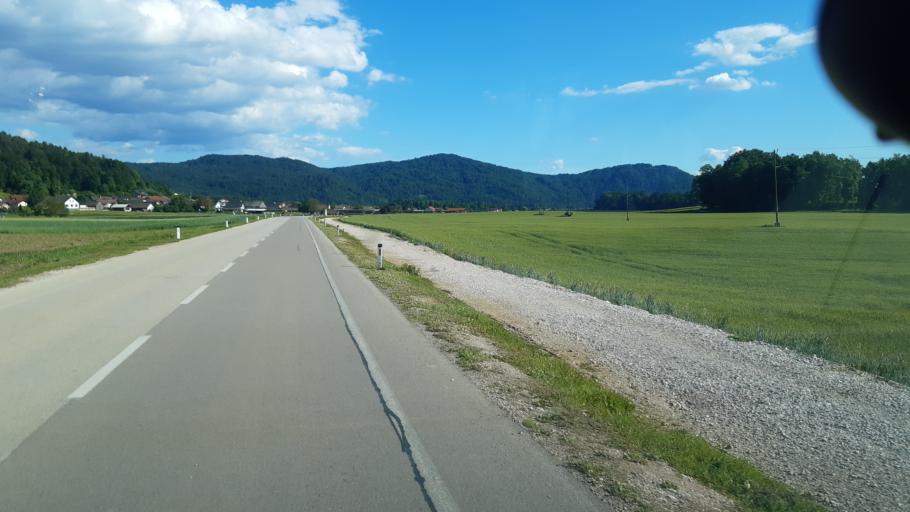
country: SI
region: Vodice
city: Vodice
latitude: 46.1811
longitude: 14.5023
